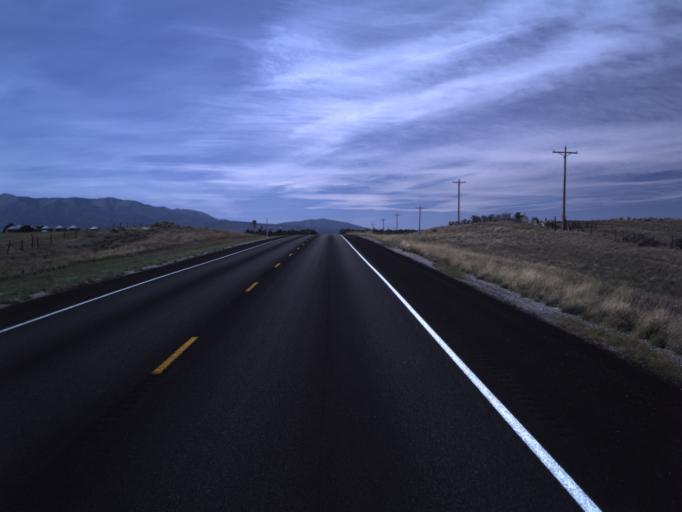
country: US
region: Utah
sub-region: San Juan County
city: Monticello
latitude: 37.8535
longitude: -109.1793
